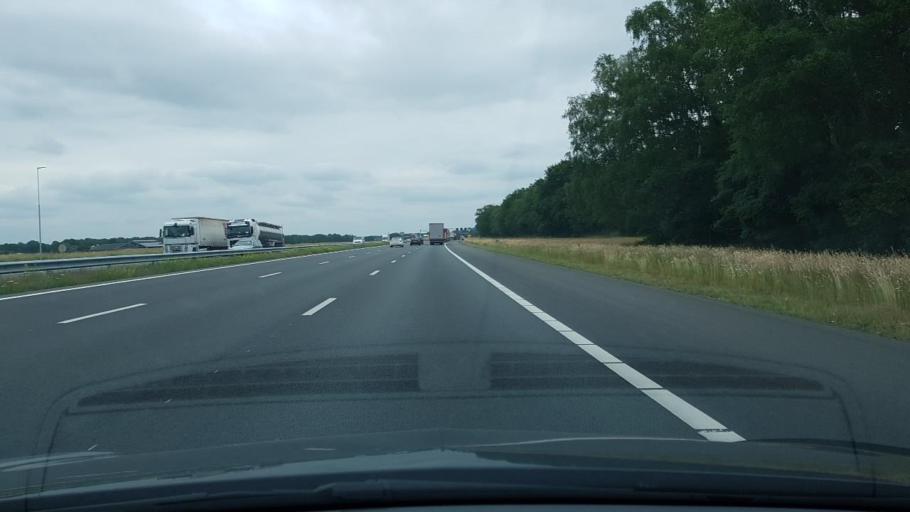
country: NL
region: Gelderland
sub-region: Gemeente Lochem
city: Laren
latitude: 52.2459
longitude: 6.3578
